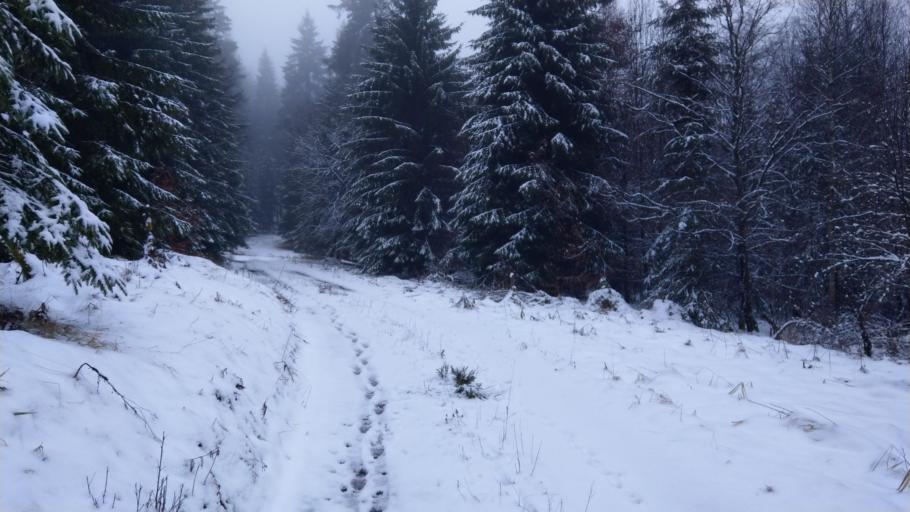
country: DE
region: North Rhine-Westphalia
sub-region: Regierungsbezirk Arnsberg
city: Erndtebruck
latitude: 50.9815
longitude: 8.1899
